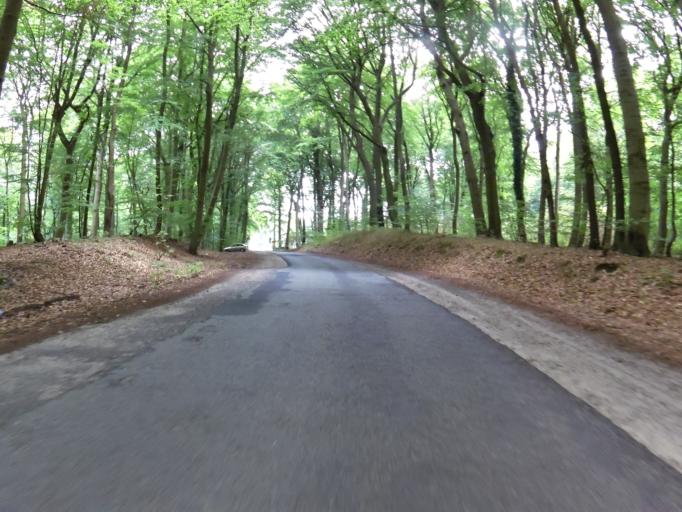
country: DE
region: Mecklenburg-Vorpommern
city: Seebad Heringsdorf
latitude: 53.9515
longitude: 14.1597
